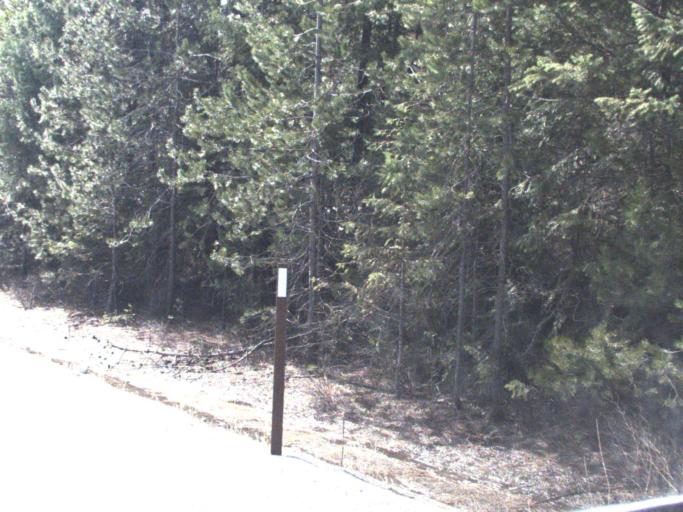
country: US
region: Washington
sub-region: Stevens County
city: Colville
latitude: 48.5155
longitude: -117.6847
